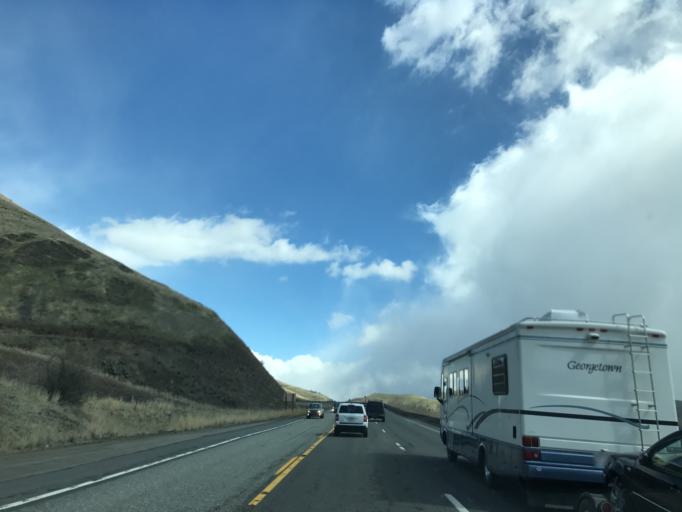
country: US
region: Idaho
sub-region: Idaho County
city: Grangeville
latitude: 45.8053
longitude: -116.2842
